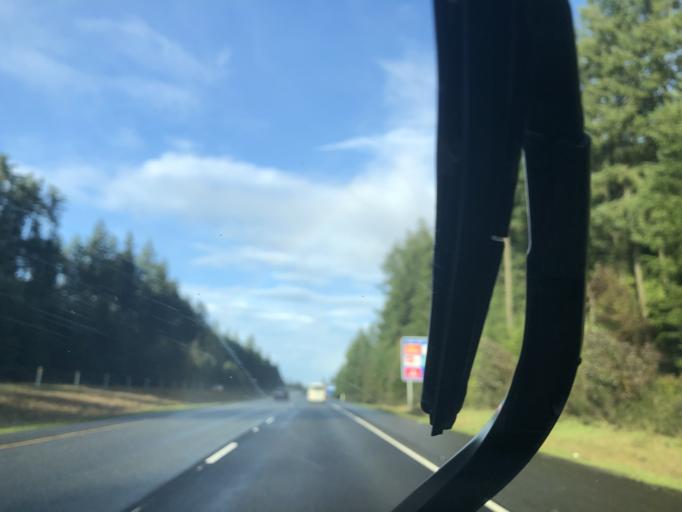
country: US
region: Washington
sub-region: Kitsap County
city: Poulsbo
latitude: 47.7378
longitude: -122.6735
